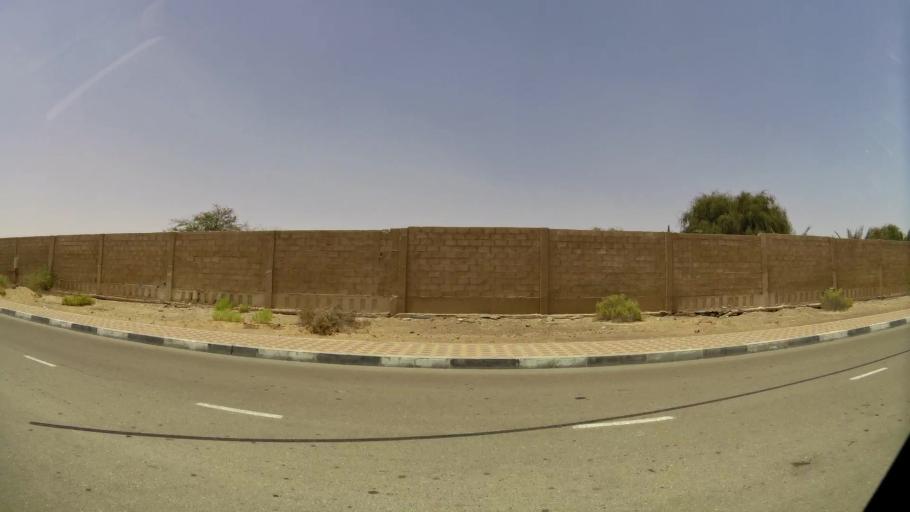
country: OM
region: Al Buraimi
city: Al Buraymi
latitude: 24.2683
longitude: 55.7074
